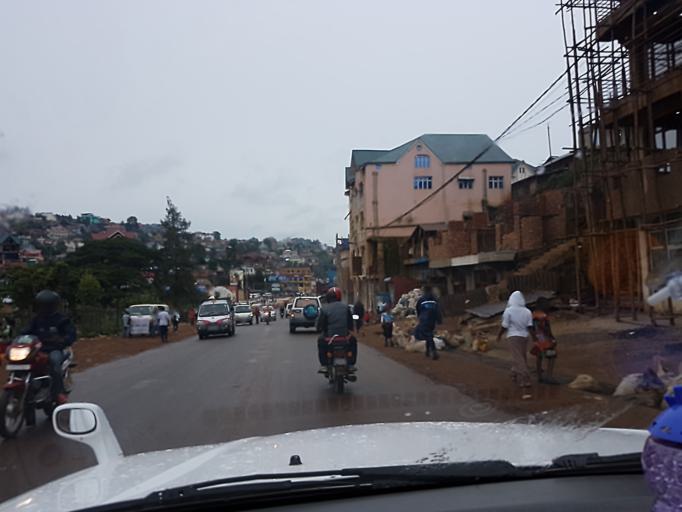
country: CD
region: South Kivu
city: Bukavu
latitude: -2.4989
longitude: 28.8509
